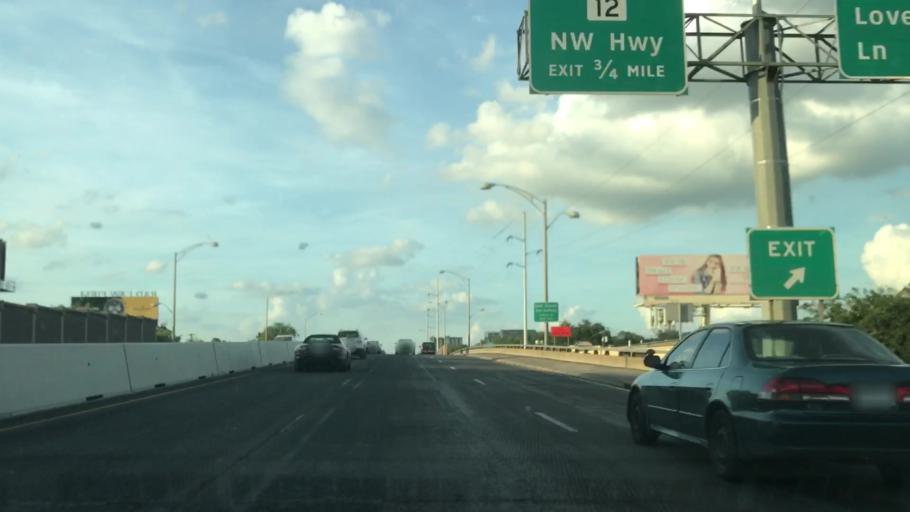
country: US
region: Texas
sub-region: Dallas County
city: University Park
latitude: 32.8500
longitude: -96.8133
